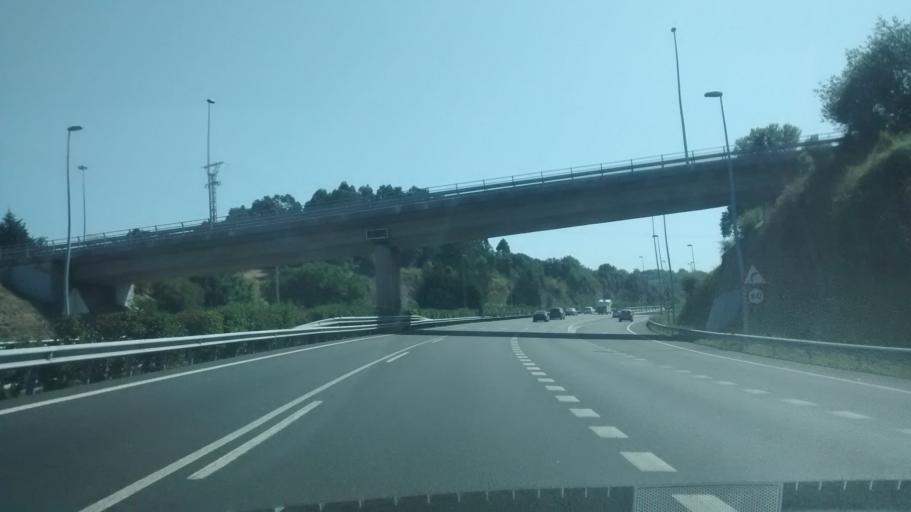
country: ES
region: Cantabria
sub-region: Provincia de Cantabria
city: Laredo
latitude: 43.4047
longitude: -3.4131
